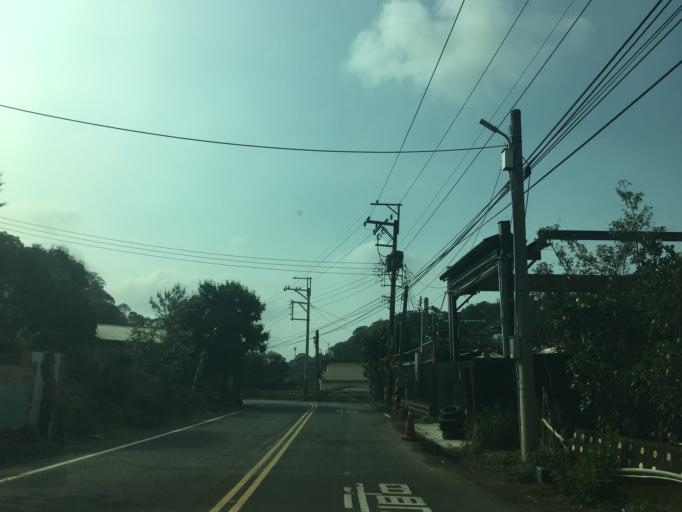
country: TW
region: Taiwan
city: Fengyuan
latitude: 24.2239
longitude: 120.7574
